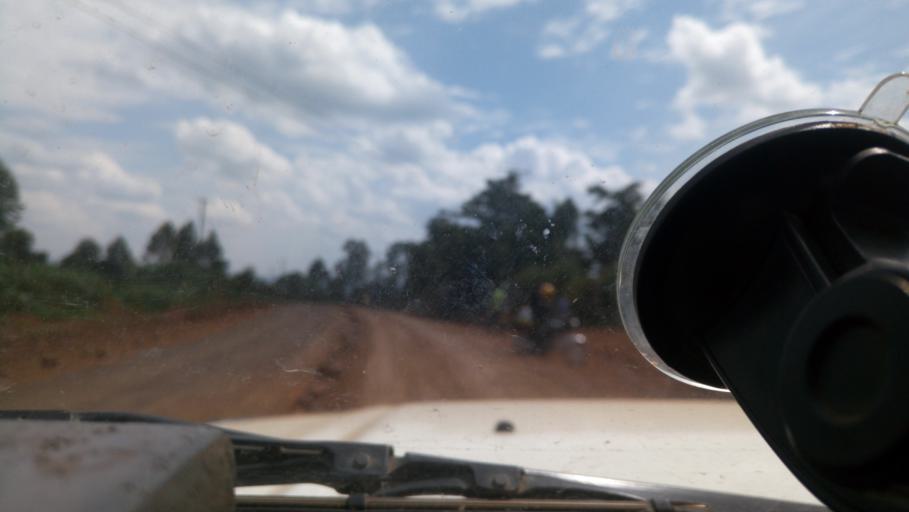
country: KE
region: Kericho
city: Litein
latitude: -0.5817
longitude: 35.1349
